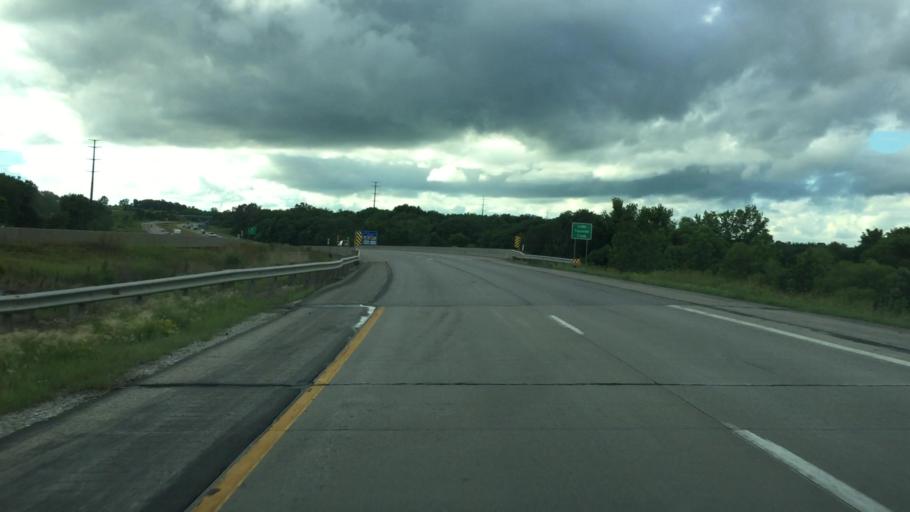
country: US
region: Iowa
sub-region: Polk County
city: Altoona
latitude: 41.6226
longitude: -93.4936
